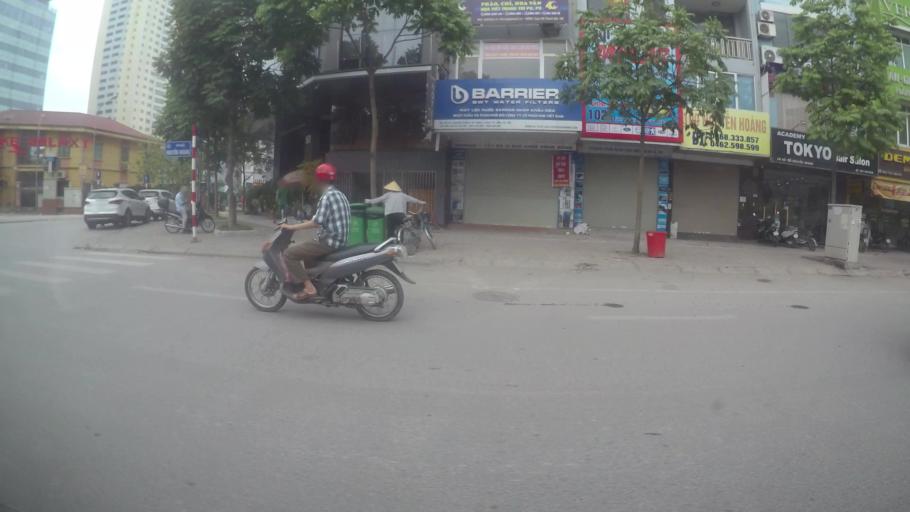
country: VN
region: Ha Noi
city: Cau Dien
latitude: 21.0330
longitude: 105.7724
